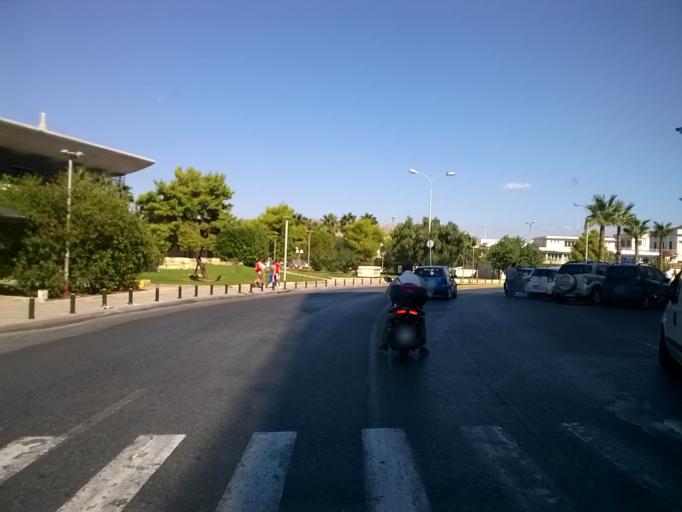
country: GR
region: Attica
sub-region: Nomos Attikis
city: Piraeus
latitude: 37.9383
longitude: 23.6394
